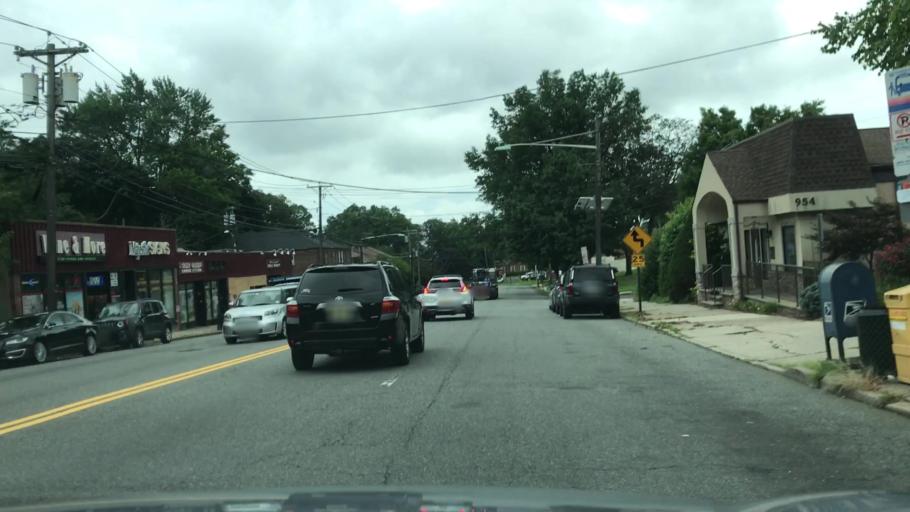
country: US
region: New Jersey
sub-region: Bergen County
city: Teaneck
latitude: 40.8881
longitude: -74.0054
